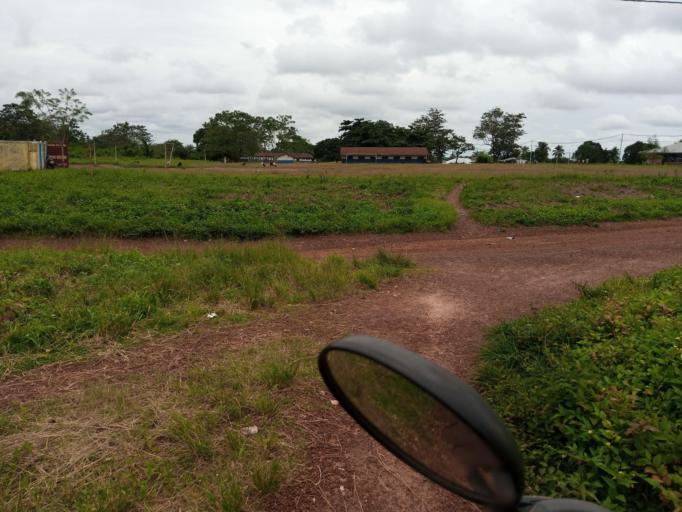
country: SL
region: Southern Province
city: Largo
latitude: 8.2007
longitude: -12.0611
